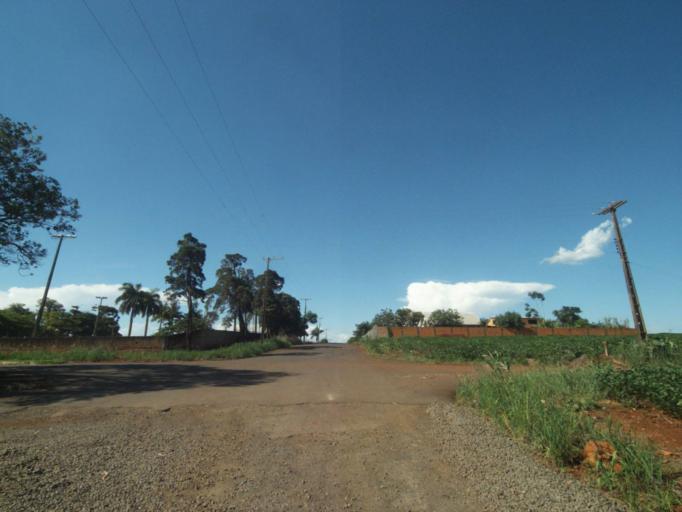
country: BR
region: Parana
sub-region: Sertanopolis
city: Sertanopolis
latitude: -23.0429
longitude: -50.8138
